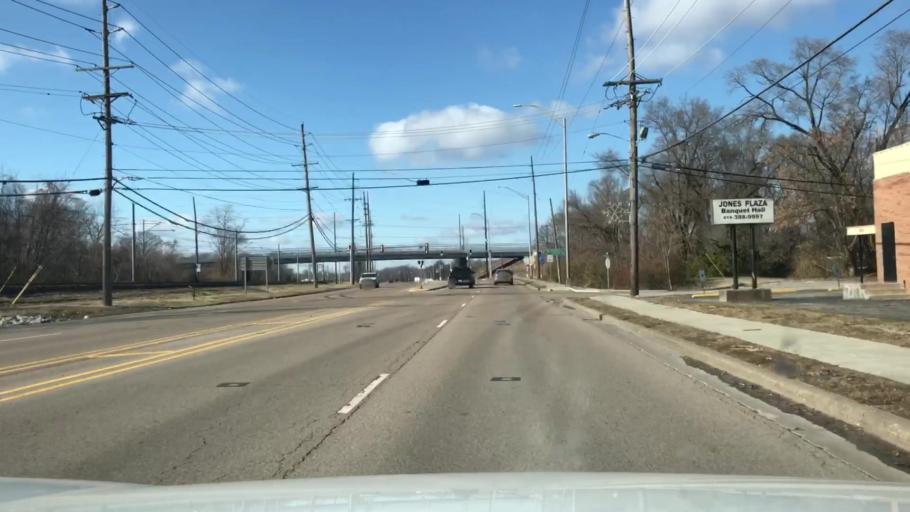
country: US
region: Illinois
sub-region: Saint Clair County
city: Caseyville
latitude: 38.5975
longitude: -90.0506
